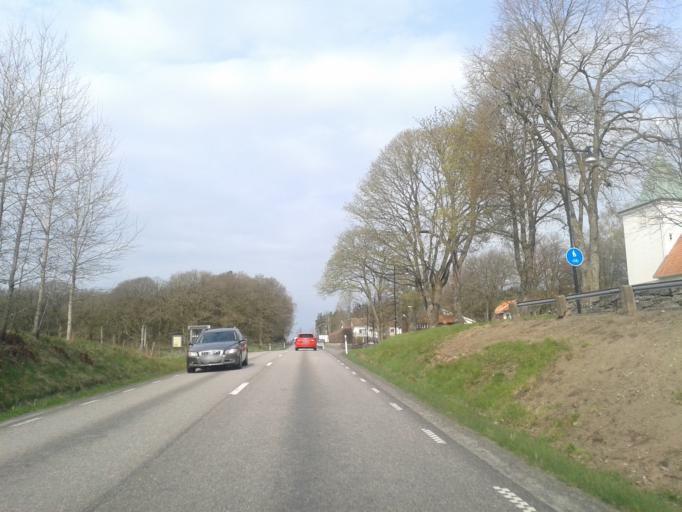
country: SE
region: Vaestra Goetaland
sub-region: Kungalvs Kommun
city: Kode
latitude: 57.8951
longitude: 11.8288
